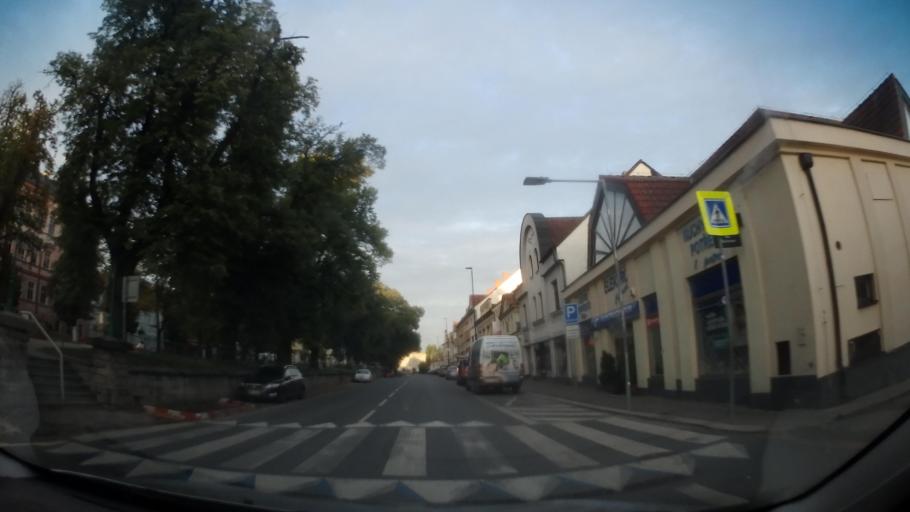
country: CZ
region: Central Bohemia
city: Lysa nad Labem
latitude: 50.2013
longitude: 14.8391
